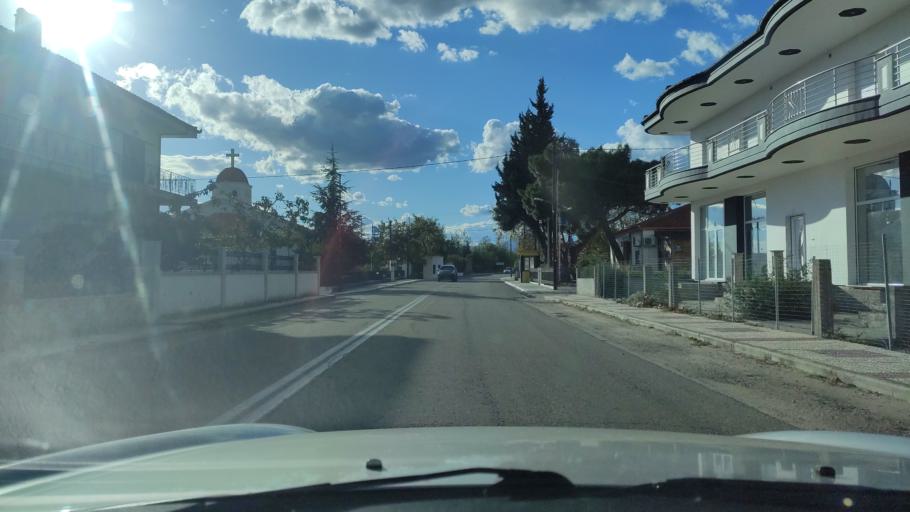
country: GR
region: East Macedonia and Thrace
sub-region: Nomos Xanthis
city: Selero
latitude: 41.1225
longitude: 25.0646
